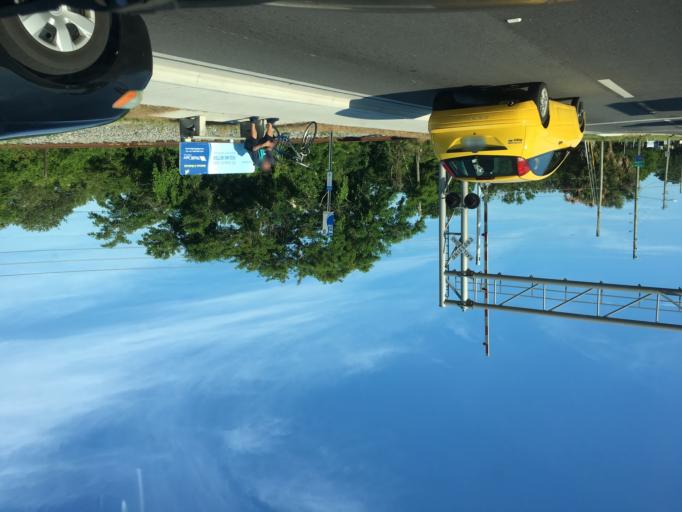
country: US
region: Florida
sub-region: Pinellas County
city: West and East Lealman
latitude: 27.8278
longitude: -82.7000
